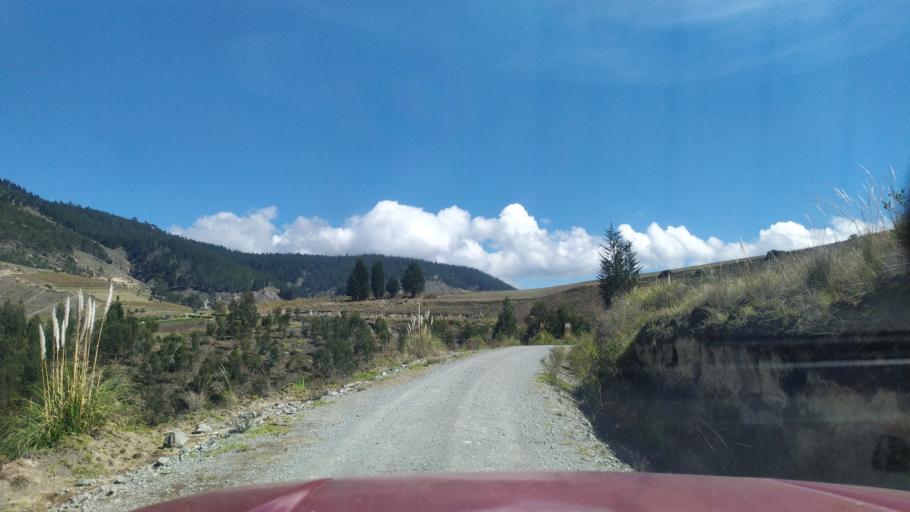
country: EC
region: Chimborazo
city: Riobamba
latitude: -1.6752
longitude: -78.6993
